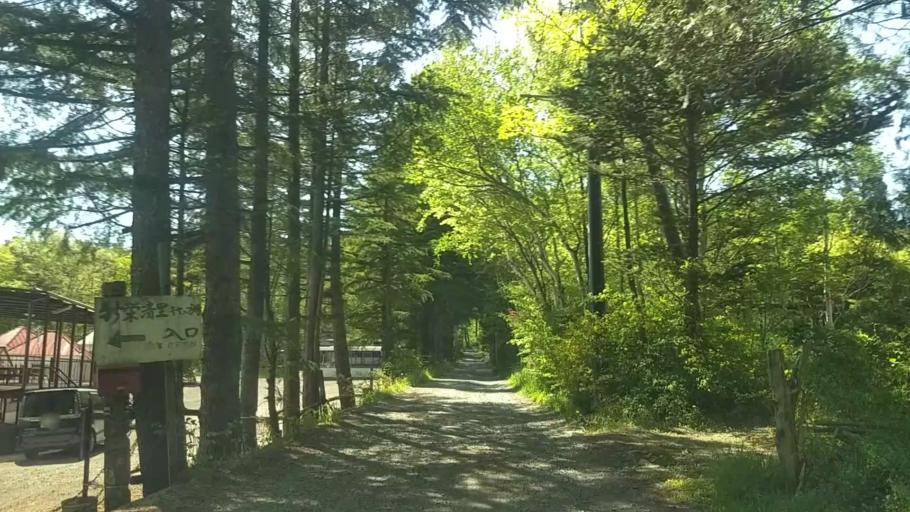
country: JP
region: Yamanashi
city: Nirasaki
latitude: 35.9120
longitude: 138.4323
